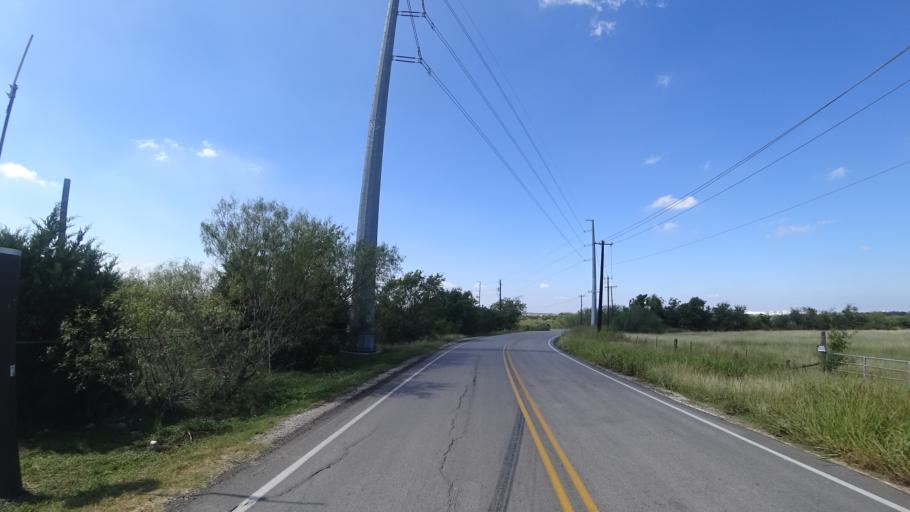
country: US
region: Texas
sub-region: Travis County
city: Manor
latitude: 30.3499
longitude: -97.6302
